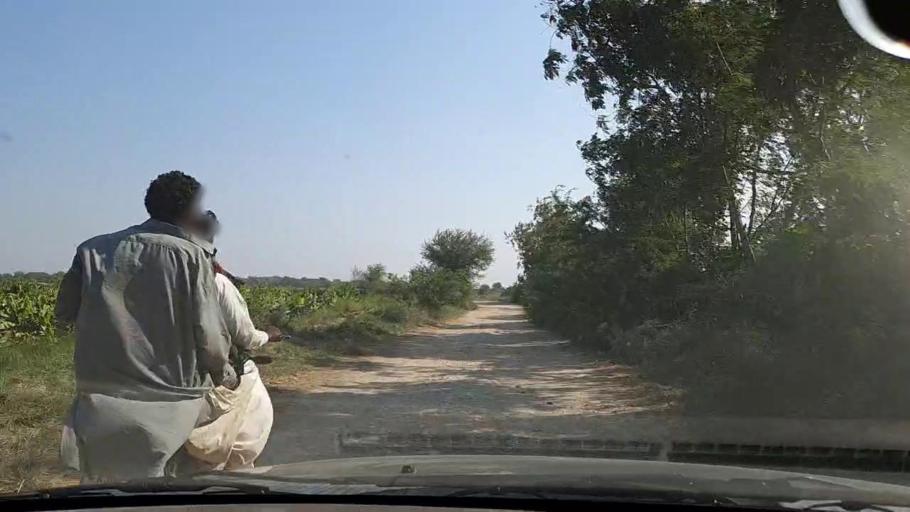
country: PK
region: Sindh
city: Chuhar Jamali
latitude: 24.4180
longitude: 67.8297
